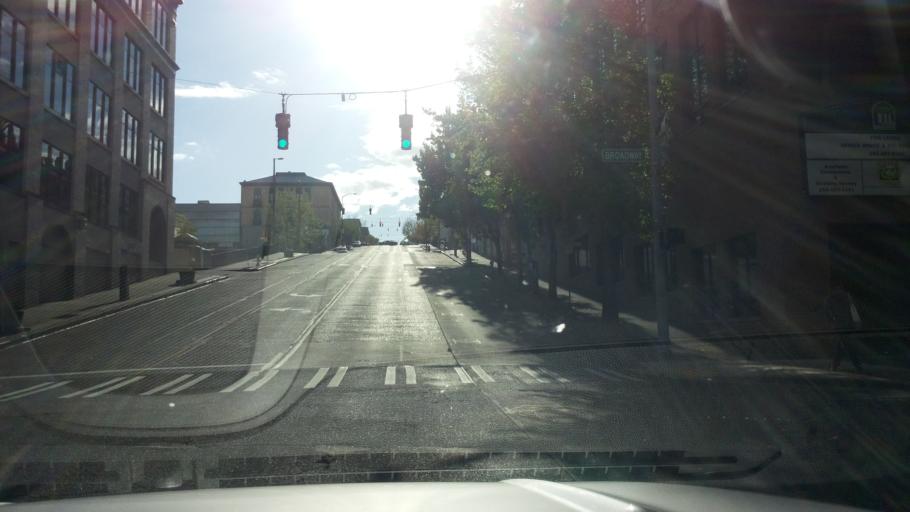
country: US
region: Washington
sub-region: Pierce County
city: Tacoma
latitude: 47.2533
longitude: -122.4400
